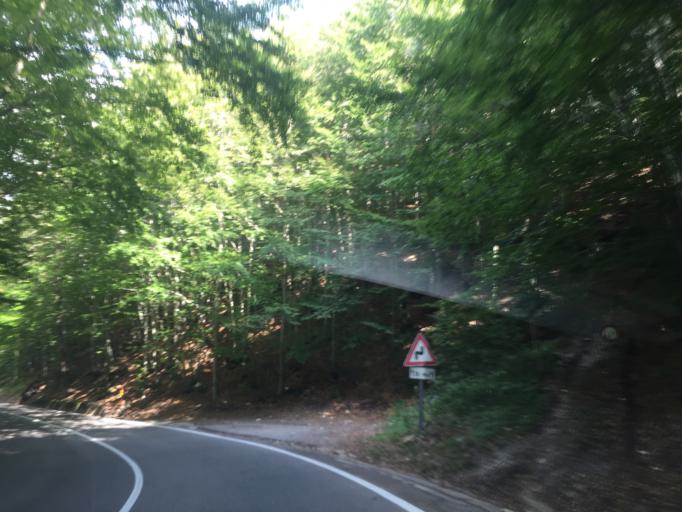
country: IT
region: Tuscany
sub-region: Provincia di Pistoia
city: Abetone
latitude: 44.1251
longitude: 10.7080
